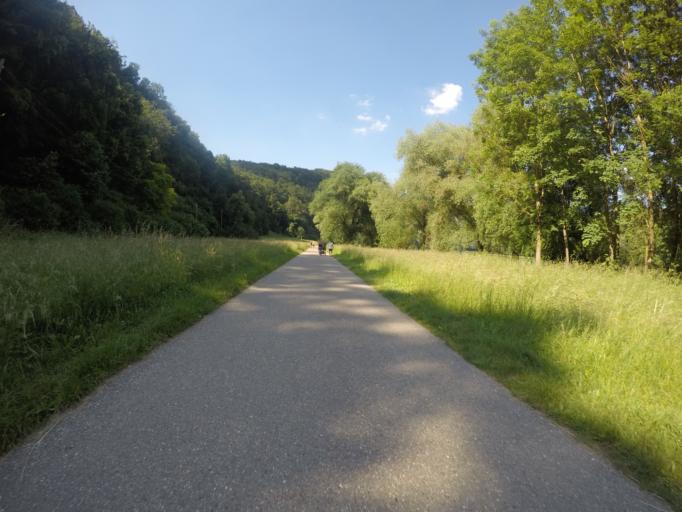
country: DE
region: Bavaria
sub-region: Lower Bavaria
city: Ihrlerstein
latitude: 48.9117
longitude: 11.8519
